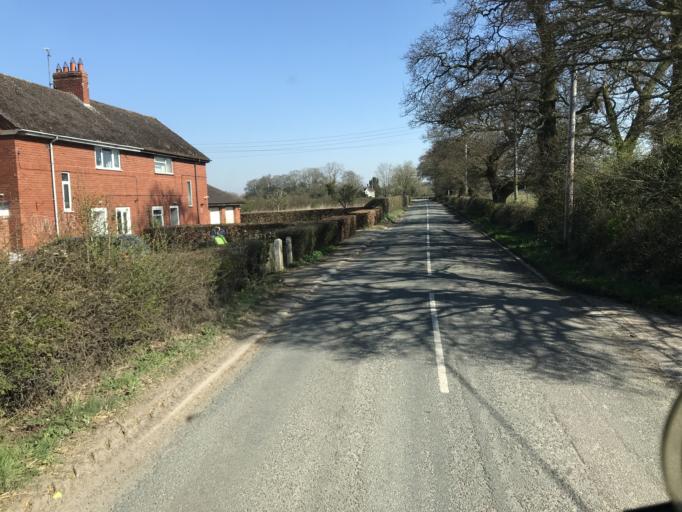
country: GB
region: England
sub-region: Cheshire West and Chester
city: Aldford
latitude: 53.1355
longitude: -2.8458
